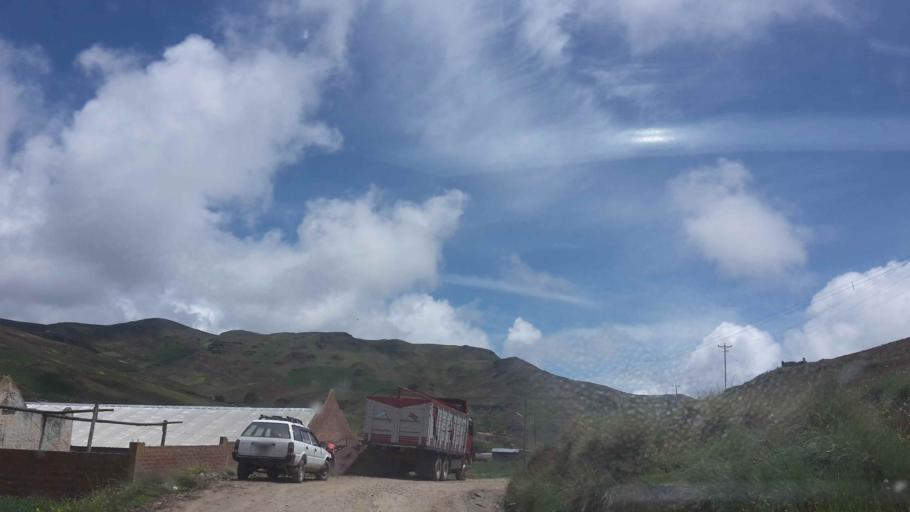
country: BO
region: Cochabamba
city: Cochabamba
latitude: -17.1938
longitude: -66.0811
